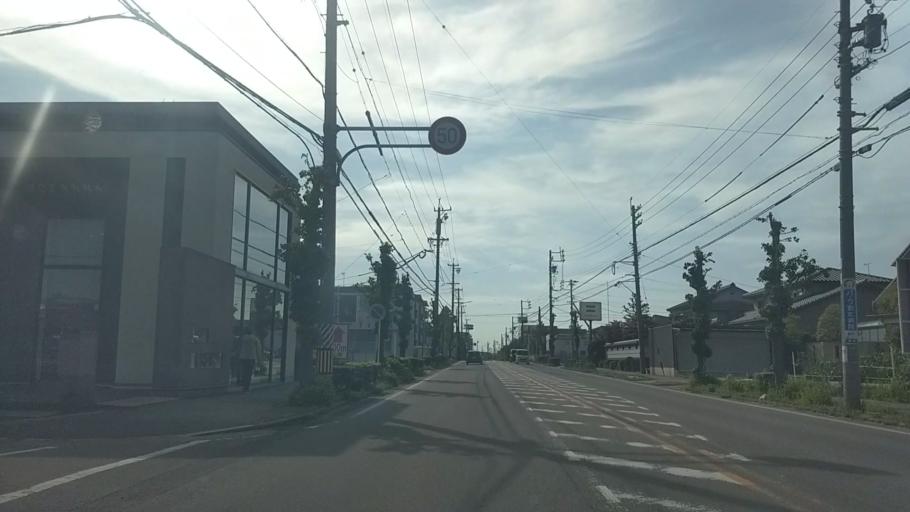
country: JP
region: Aichi
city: Anjo
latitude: 34.9509
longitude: 137.0861
